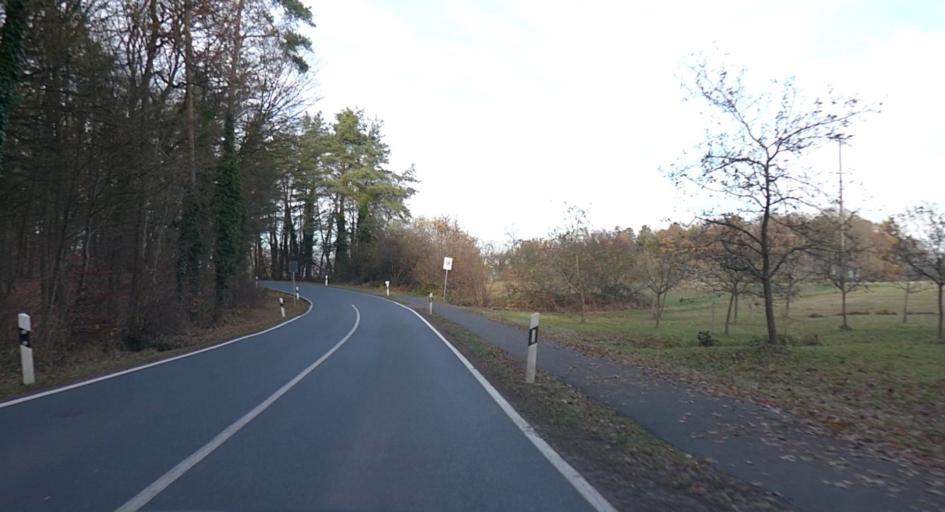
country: DE
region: Bavaria
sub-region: Regierungsbezirk Mittelfranken
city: Bubenreuth
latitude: 49.6269
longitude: 11.0393
